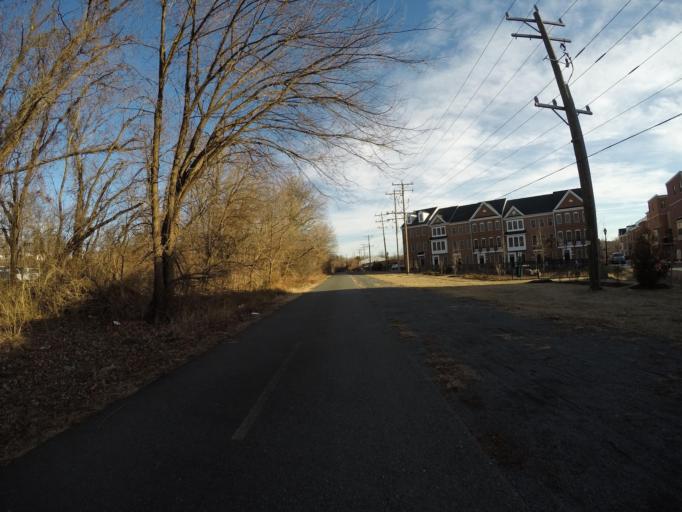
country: US
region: Virginia
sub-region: Loudoun County
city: Leesburg
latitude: 39.1092
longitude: -77.5609
